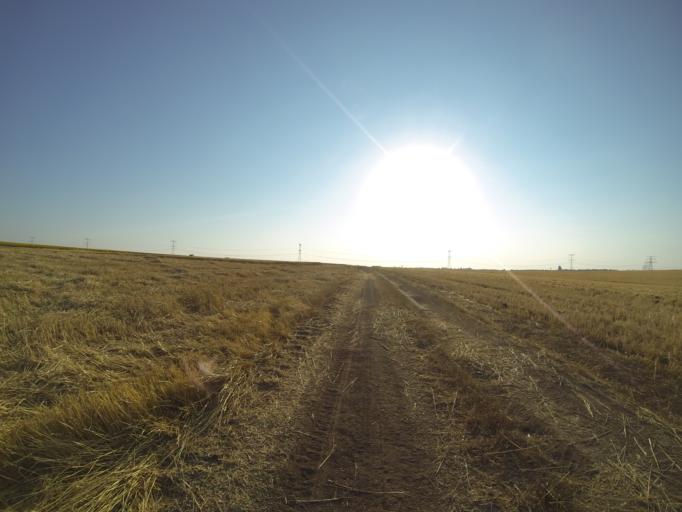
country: RO
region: Dolj
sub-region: Comuna Ceratu
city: Ceratu
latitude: 44.0284
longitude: 23.6715
